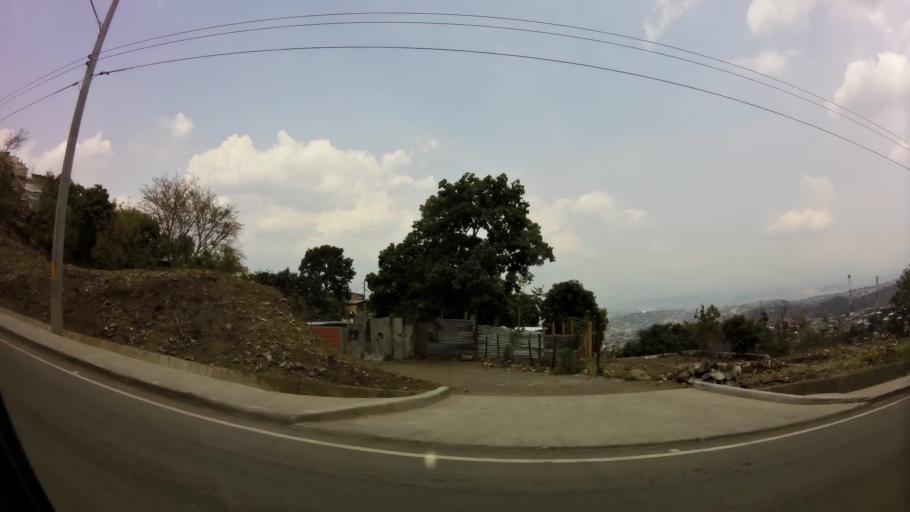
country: HN
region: Francisco Morazan
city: El Lolo
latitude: 14.1039
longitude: -87.2509
